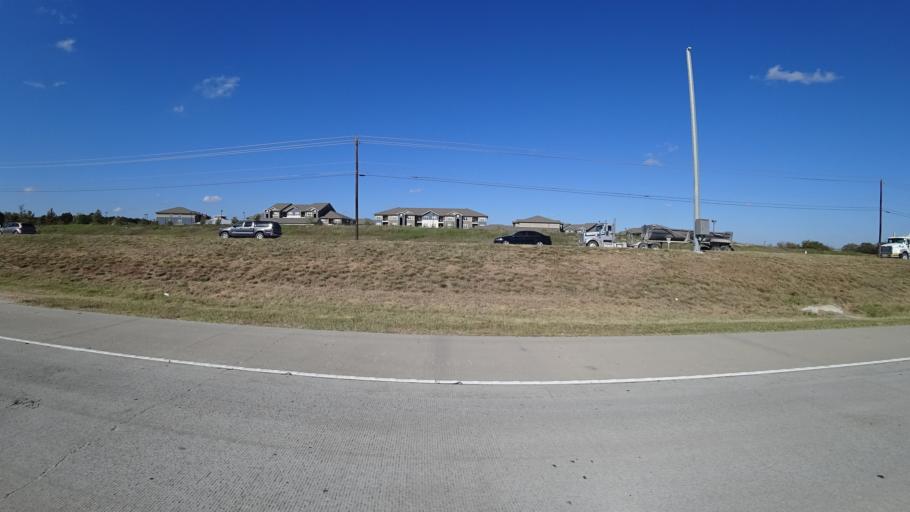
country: US
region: Texas
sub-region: Travis County
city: Austin
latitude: 30.2150
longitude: -97.7017
